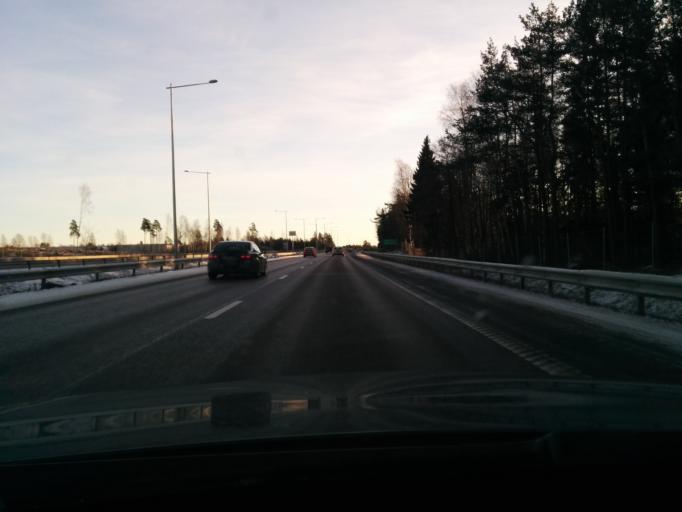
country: SE
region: Stockholm
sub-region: Upplands-Bro Kommun
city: Kungsaengen
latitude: 59.5040
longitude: 17.7324
